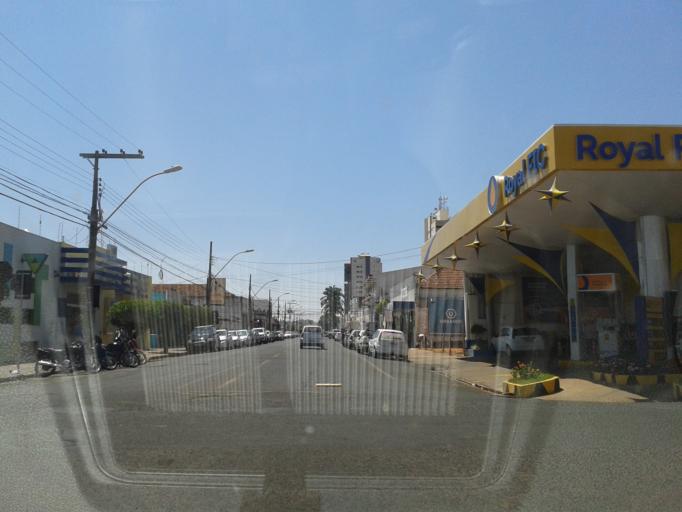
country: BR
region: Minas Gerais
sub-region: Araguari
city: Araguari
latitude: -18.6525
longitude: -48.1912
